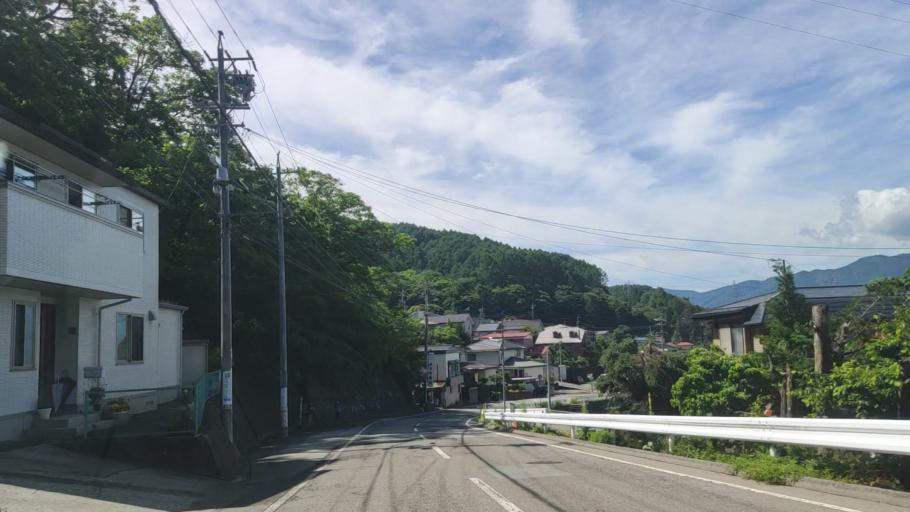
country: JP
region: Nagano
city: Suwa
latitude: 36.0479
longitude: 138.1280
